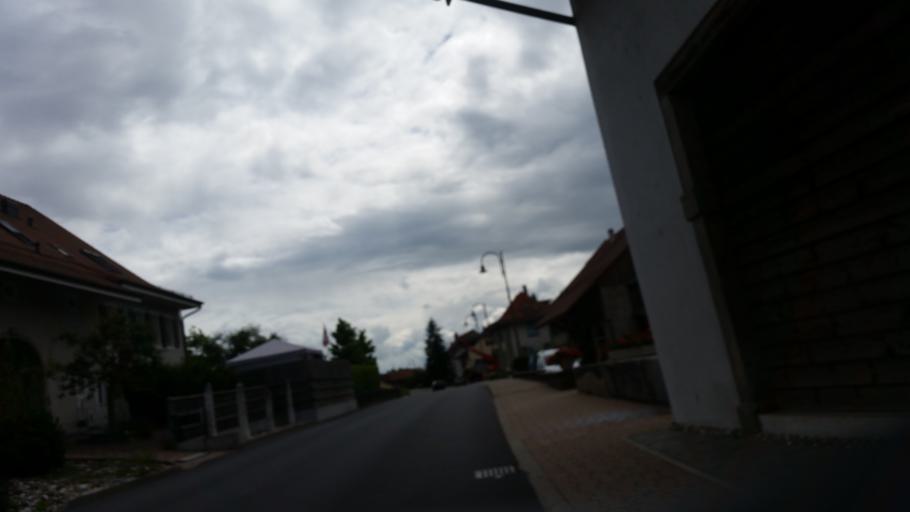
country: CH
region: Vaud
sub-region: Jura-Nord vaudois District
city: Yvonand
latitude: 46.8136
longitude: 6.7855
